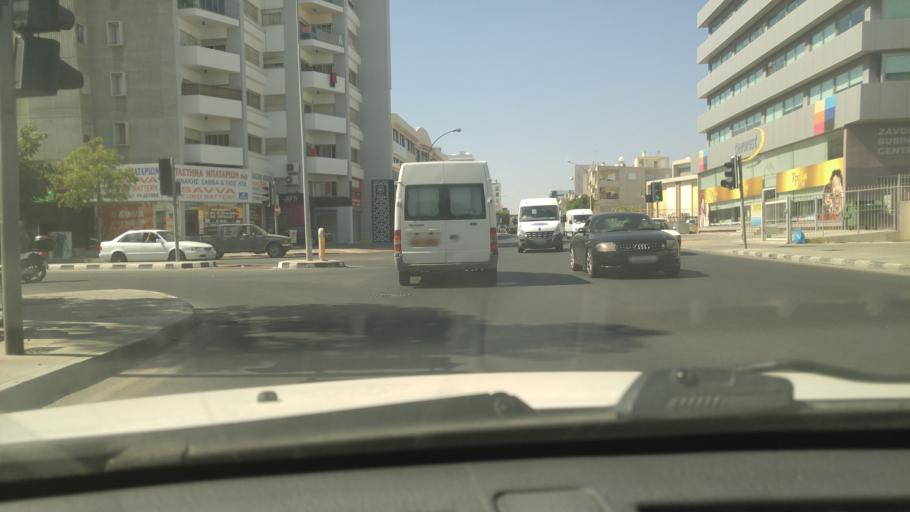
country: CY
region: Limassol
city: Limassol
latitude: 34.6737
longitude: 33.0175
